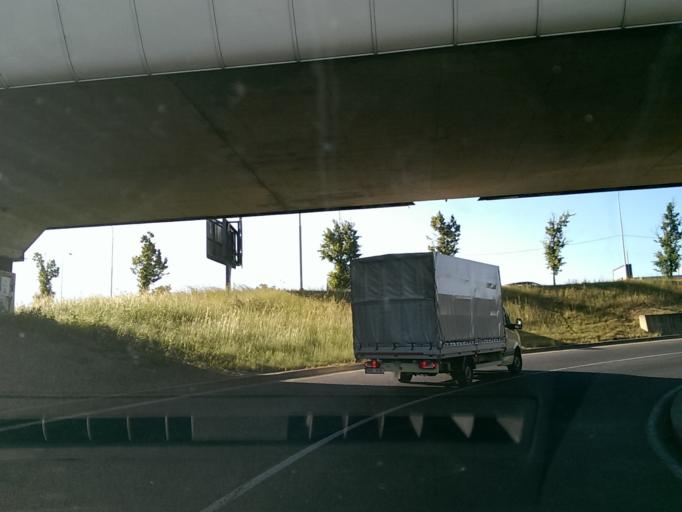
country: CZ
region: Praha
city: Cerny Most
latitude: 50.1084
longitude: 14.5734
